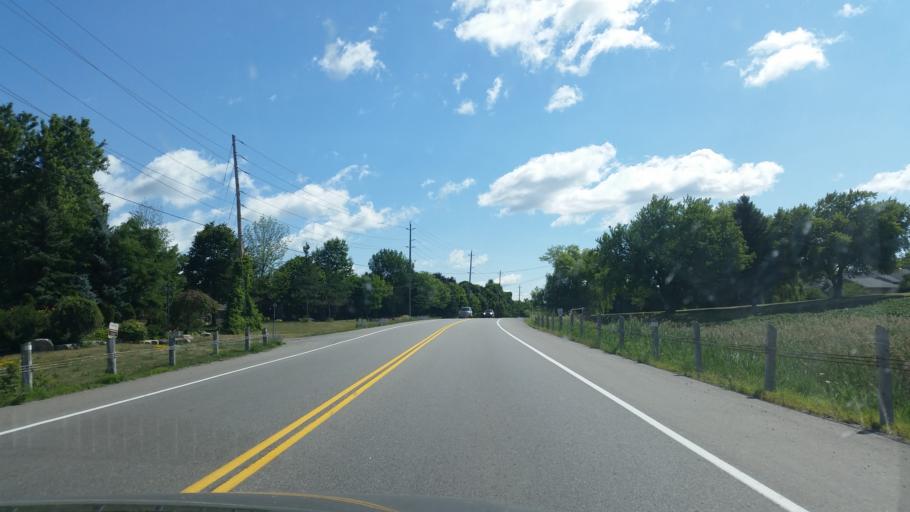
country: CA
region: Ontario
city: Vaughan
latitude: 43.8974
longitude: -79.6737
